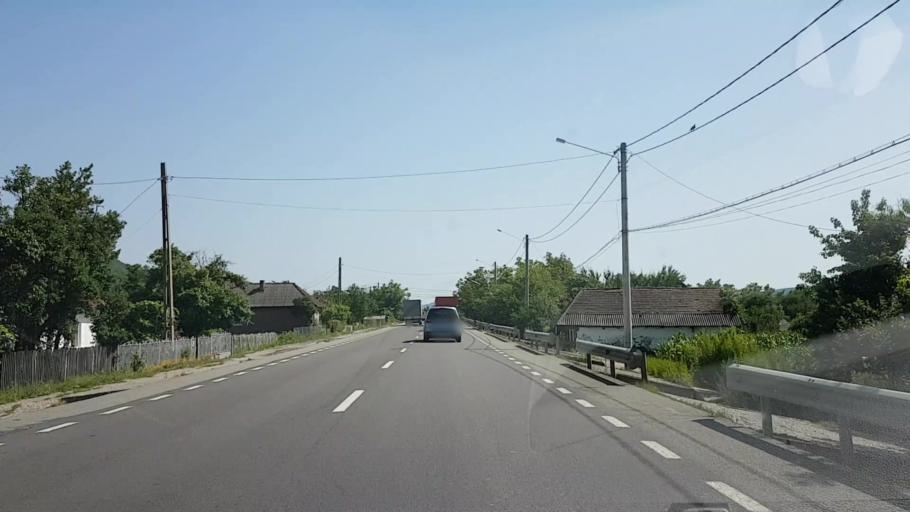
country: RO
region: Bistrita-Nasaud
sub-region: Comuna Sieu-Odorhei
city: Sieu-Odorhei
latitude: 47.1525
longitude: 24.3060
